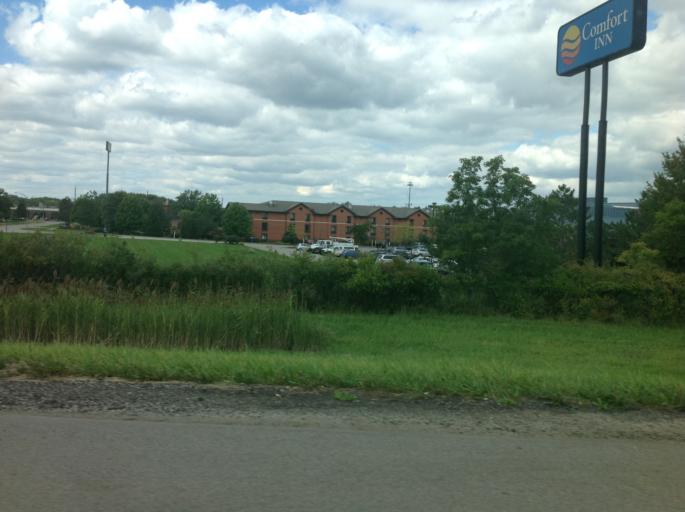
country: US
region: Ohio
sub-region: Cuyahoga County
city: Middleburg Heights
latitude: 41.3749
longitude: -81.8205
